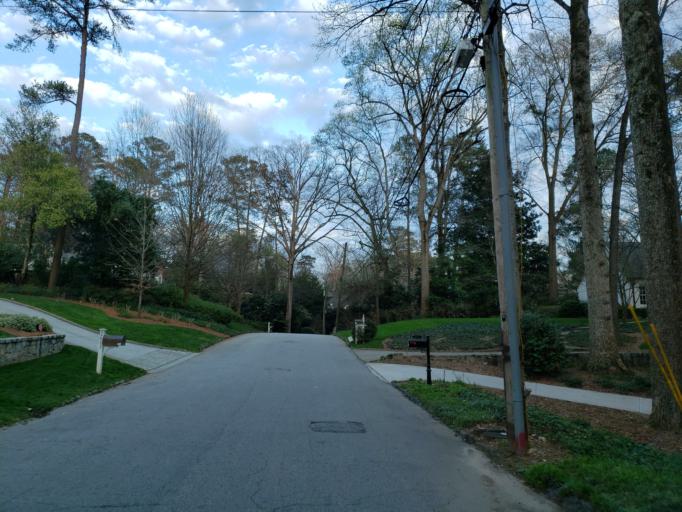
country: US
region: Georgia
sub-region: DeKalb County
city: North Atlanta
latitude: 33.8264
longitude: -84.3999
